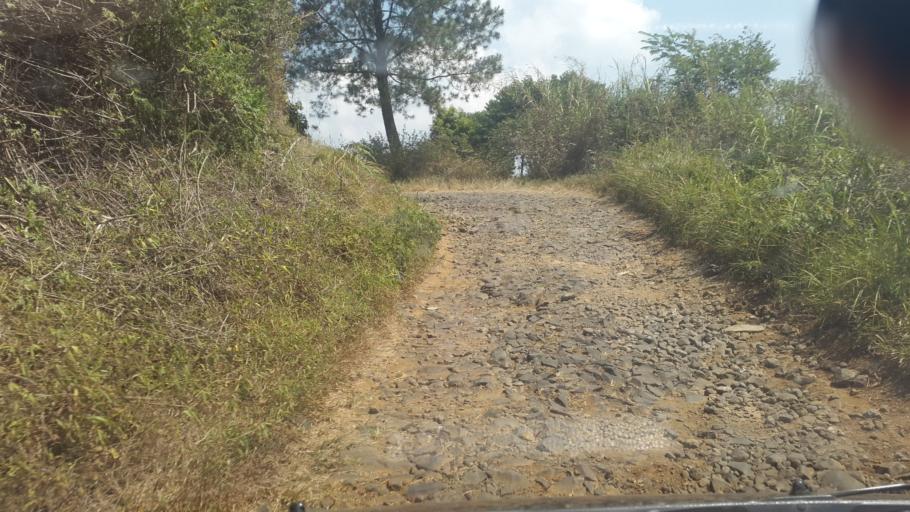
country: ID
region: West Java
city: Pasirreungit
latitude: -7.0136
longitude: 107.0138
